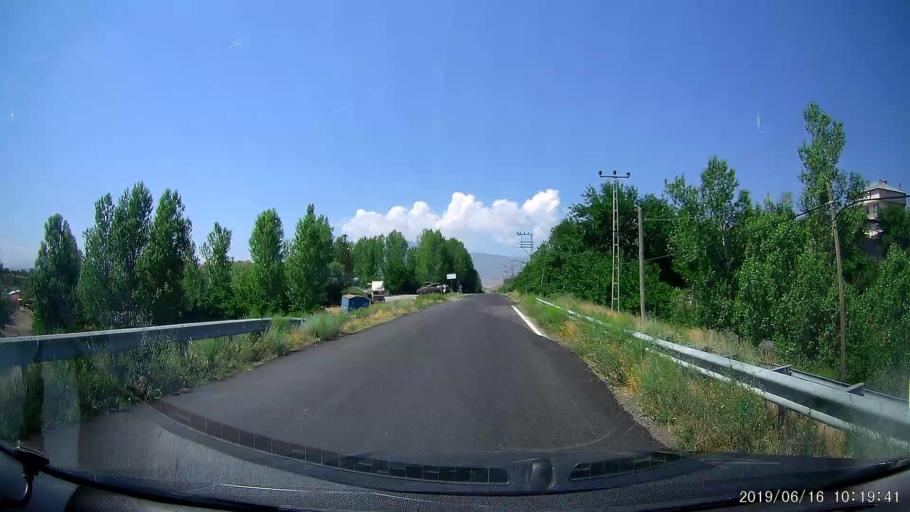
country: TR
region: Igdir
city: Tuzluca
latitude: 40.1534
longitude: 43.6542
